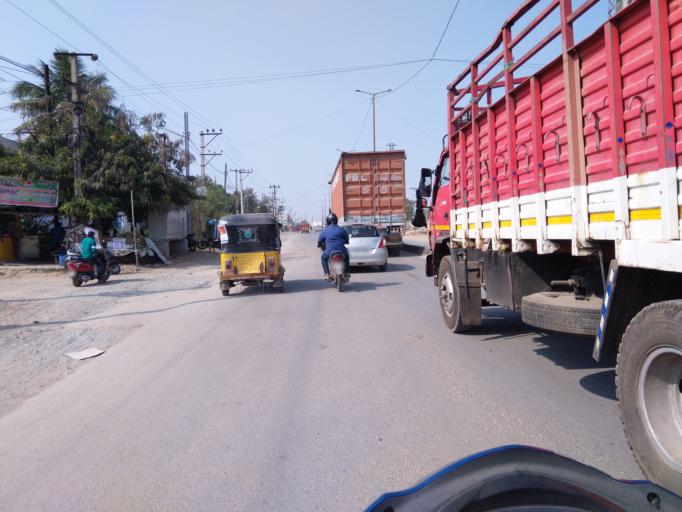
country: IN
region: Telangana
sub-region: Rangareddi
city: Quthbullapur
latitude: 17.5340
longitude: 78.4355
